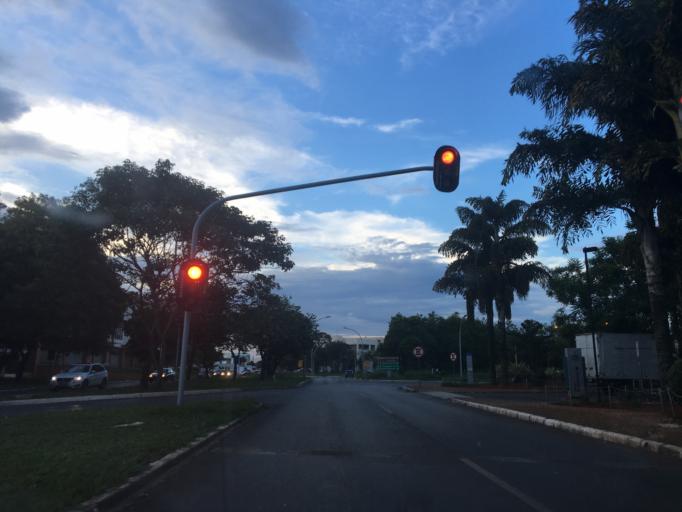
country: BR
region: Federal District
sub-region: Brasilia
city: Brasilia
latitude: -15.7983
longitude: -47.8953
